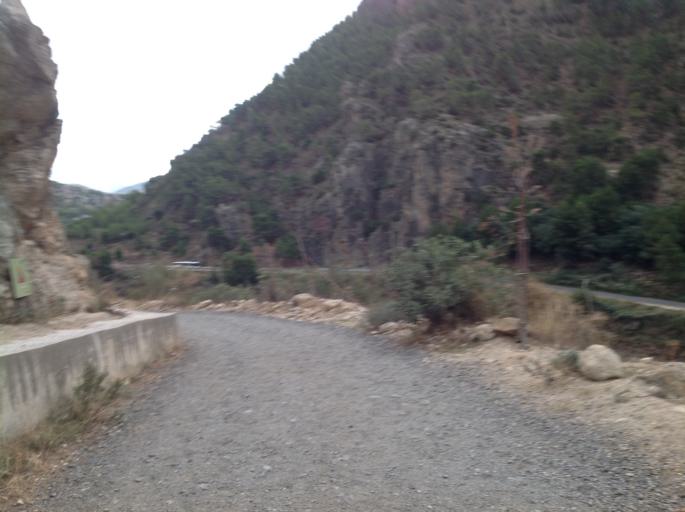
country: ES
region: Andalusia
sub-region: Provincia de Malaga
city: Carratraca
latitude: 36.9128
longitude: -4.7684
